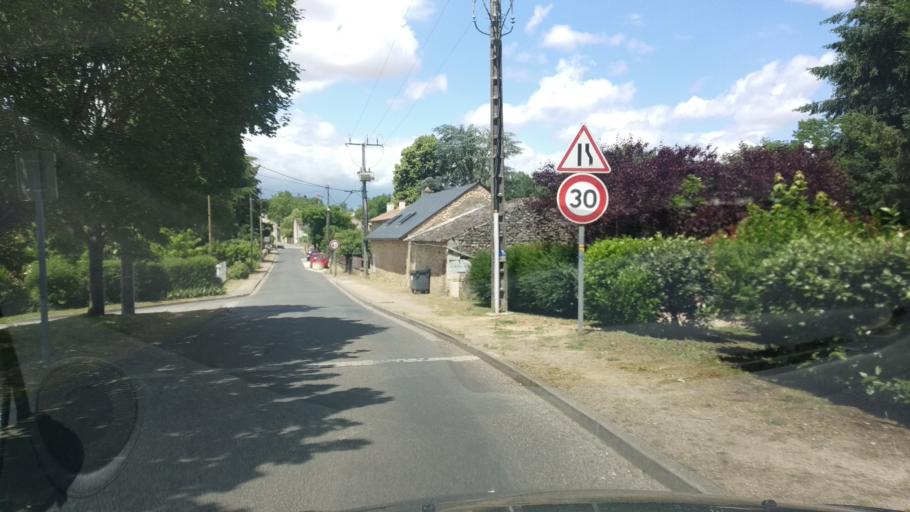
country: FR
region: Poitou-Charentes
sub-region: Departement de la Vienne
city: Cisse
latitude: 46.6045
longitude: 0.2396
